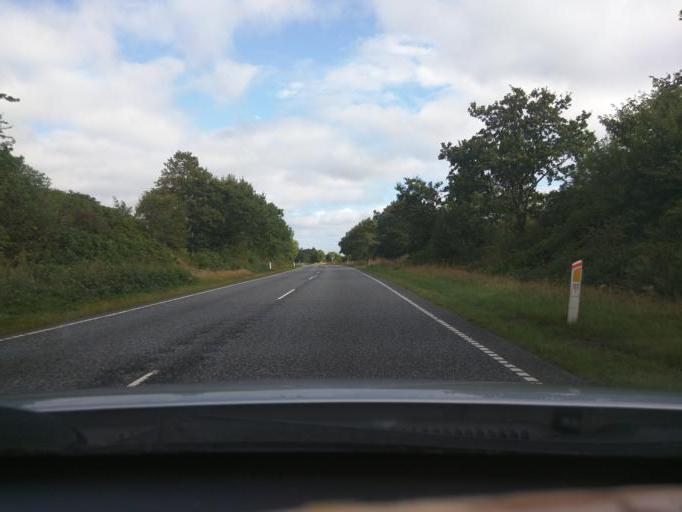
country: DK
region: Central Jutland
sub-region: Viborg Kommune
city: Viborg
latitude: 56.3776
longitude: 9.3794
